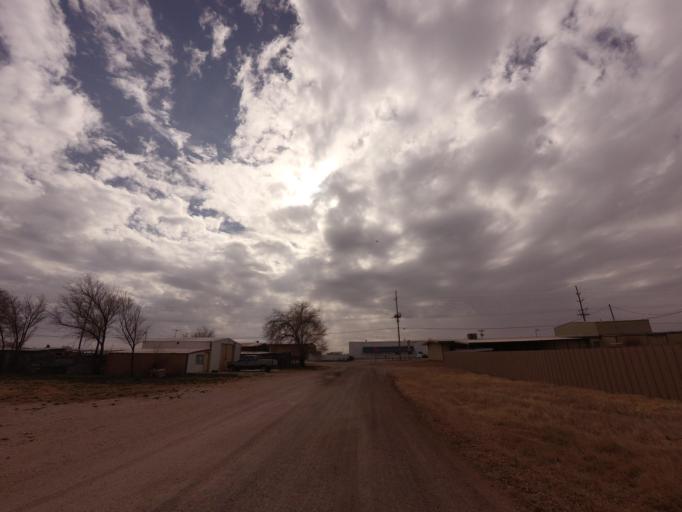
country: US
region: New Mexico
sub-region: Curry County
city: Clovis
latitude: 34.3908
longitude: -103.2155
